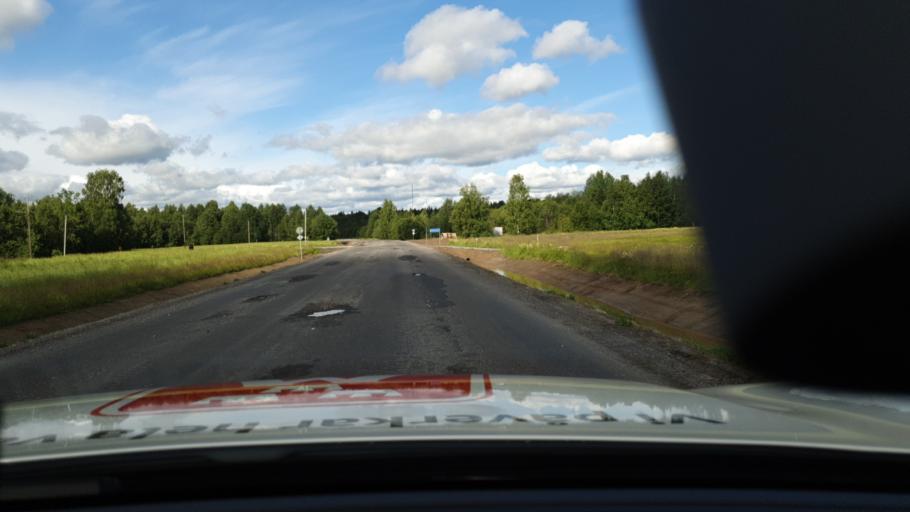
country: SE
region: Norrbotten
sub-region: Bodens Kommun
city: Boden
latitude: 65.8511
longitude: 21.5631
